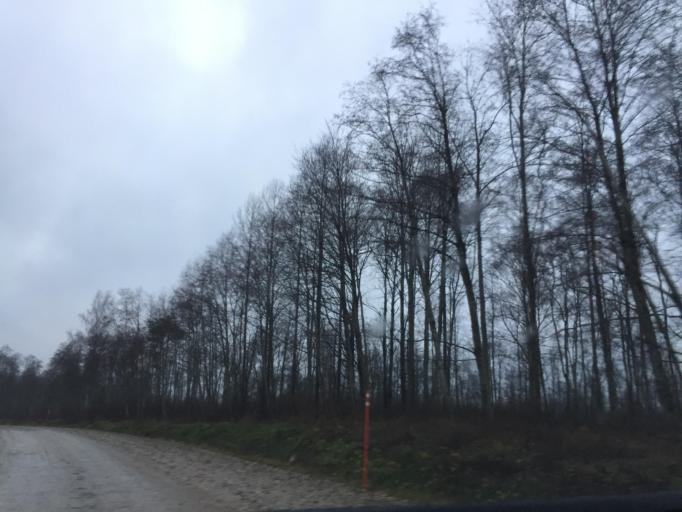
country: LV
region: Salacgrivas
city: Salacgriva
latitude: 57.7672
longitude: 24.4721
